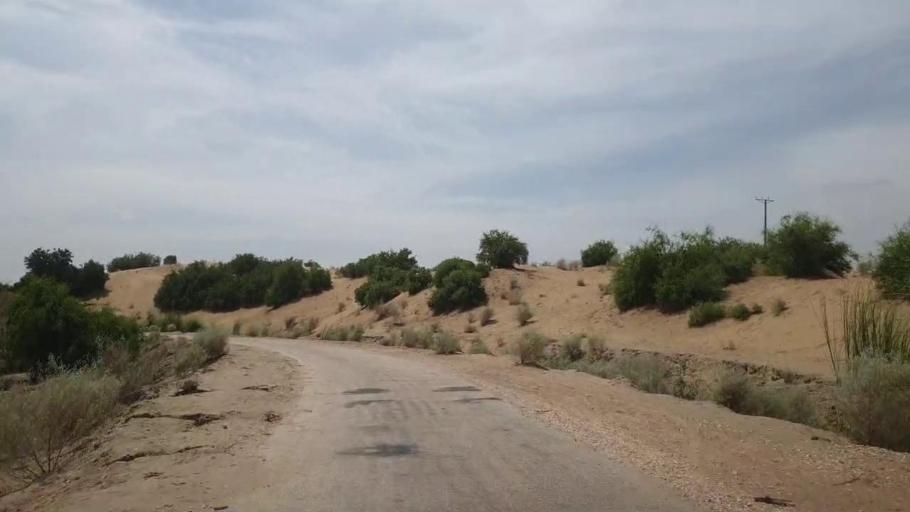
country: PK
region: Sindh
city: Kot Diji
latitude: 27.1059
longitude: 69.0771
